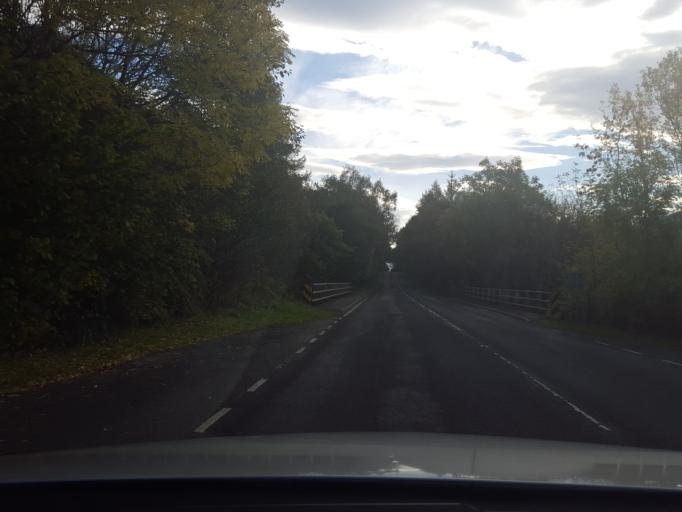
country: GB
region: Scotland
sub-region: Highland
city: Fort William
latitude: 57.2506
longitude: -5.4727
